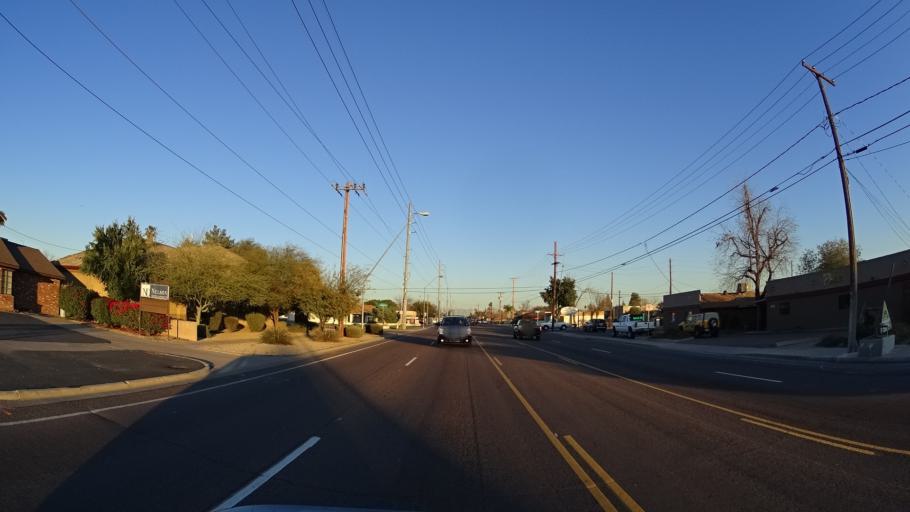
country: US
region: Arizona
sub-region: Maricopa County
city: Mesa
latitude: 33.4224
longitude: -111.8191
